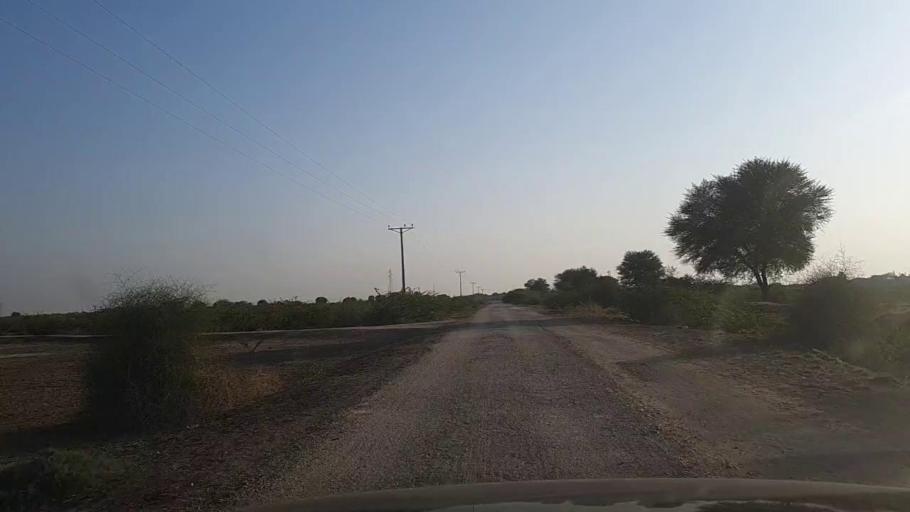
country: PK
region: Sindh
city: Naukot
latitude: 24.8924
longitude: 69.3346
